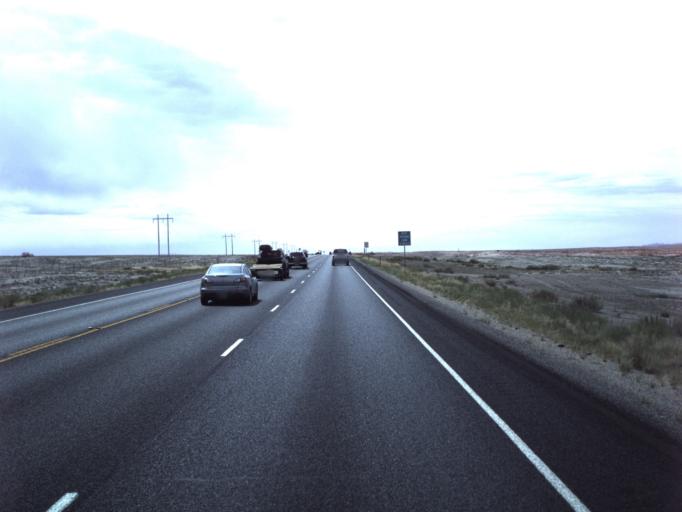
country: US
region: Utah
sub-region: Carbon County
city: East Carbon City
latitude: 39.2001
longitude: -110.3386
